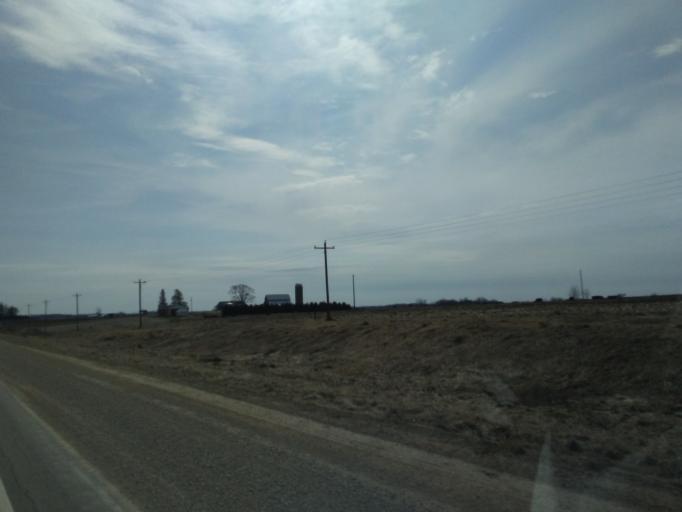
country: US
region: Iowa
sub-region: Winneshiek County
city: Decorah
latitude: 43.4409
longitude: -91.8617
